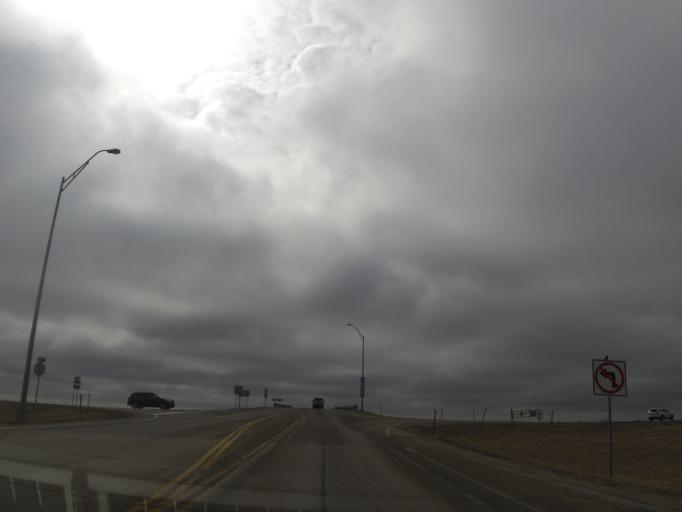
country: US
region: North Dakota
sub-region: Cass County
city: Casselton
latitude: 46.8754
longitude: -97.2108
